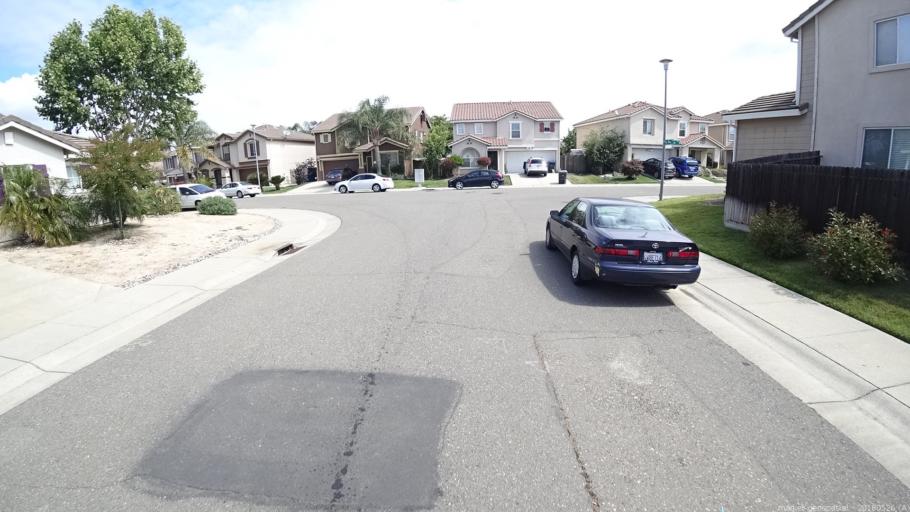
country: US
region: California
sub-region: Yolo County
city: West Sacramento
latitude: 38.6092
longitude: -121.5387
